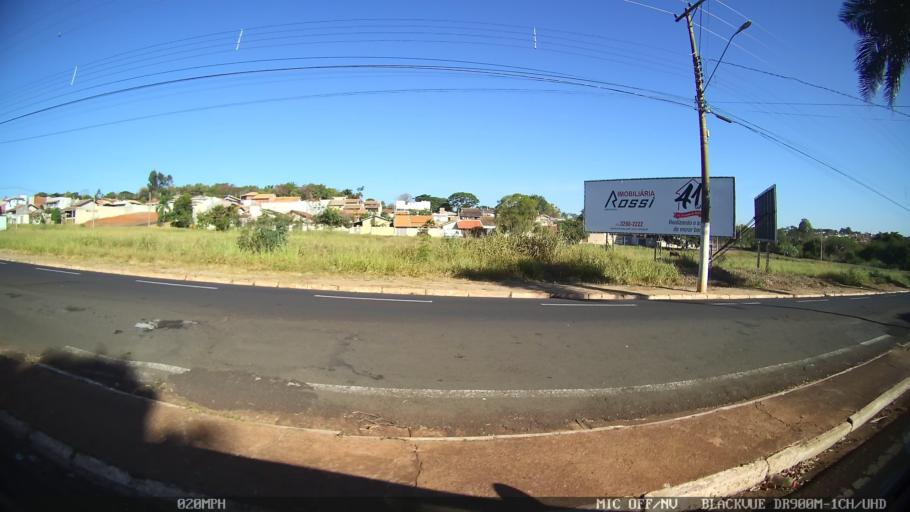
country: BR
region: Sao Paulo
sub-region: Olimpia
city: Olimpia
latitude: -20.7433
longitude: -48.9006
